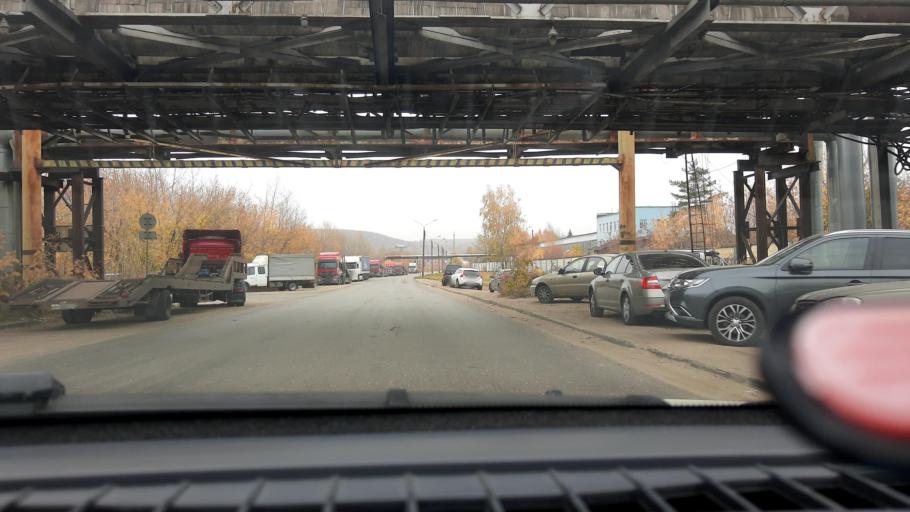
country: RU
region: Nizjnij Novgorod
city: Nizhniy Novgorod
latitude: 56.2423
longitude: 43.9033
